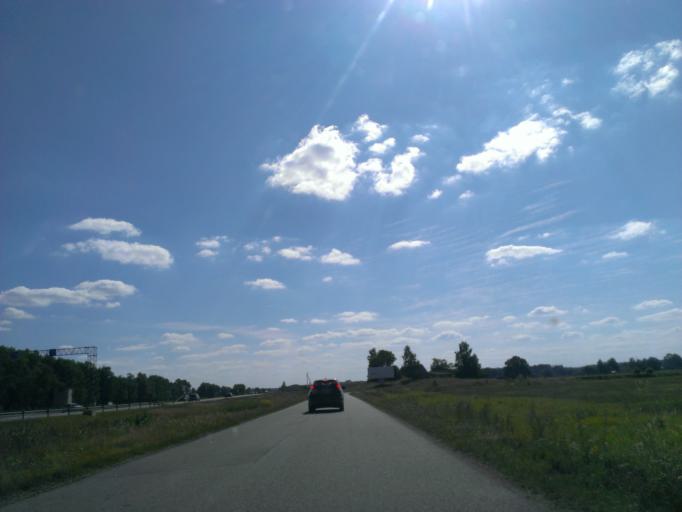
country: LV
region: Adazi
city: Adazi
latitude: 57.0960
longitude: 24.3112
